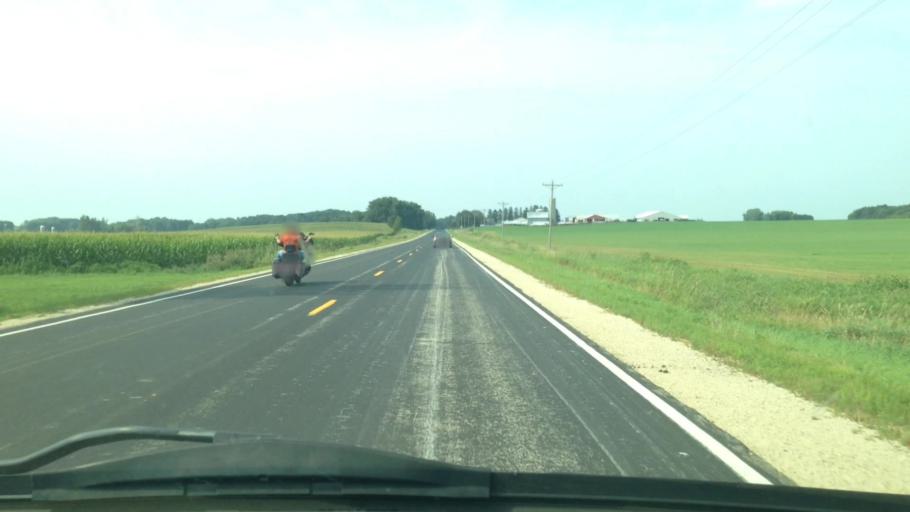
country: US
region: Minnesota
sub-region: Winona County
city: Lewiston
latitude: 43.9513
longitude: -91.9543
